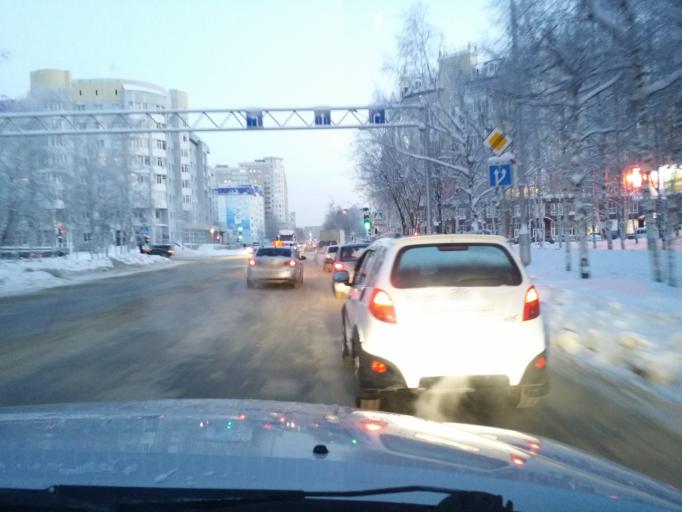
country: RU
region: Khanty-Mansiyskiy Avtonomnyy Okrug
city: Nizhnevartovsk
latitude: 60.9365
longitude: 76.5725
